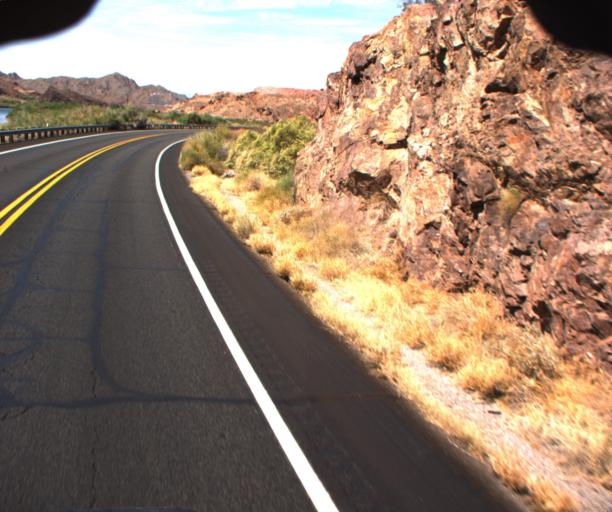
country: US
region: Arizona
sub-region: La Paz County
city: Cienega Springs
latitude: 34.2682
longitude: -114.1328
